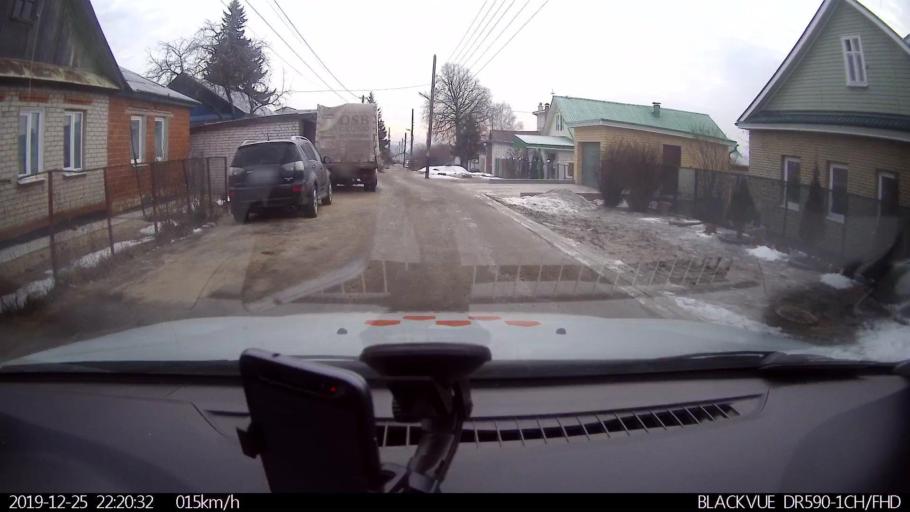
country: RU
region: Nizjnij Novgorod
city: Nizhniy Novgorod
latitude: 56.2548
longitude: 43.9953
